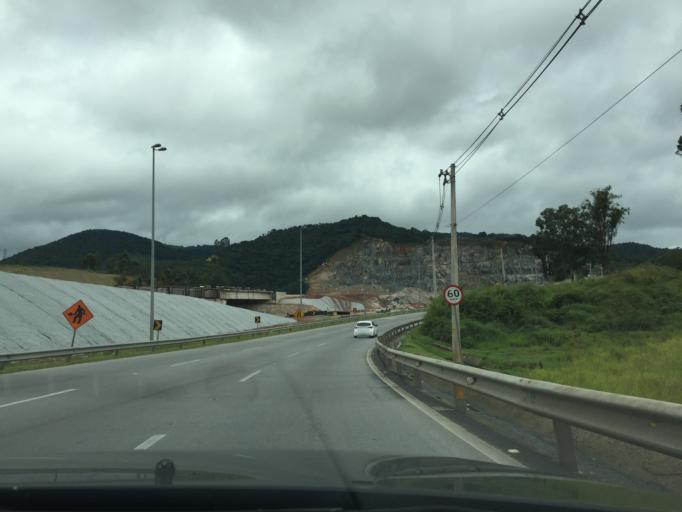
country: BR
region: Sao Paulo
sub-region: Caieiras
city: Caieiras
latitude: -23.4162
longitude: -46.7358
